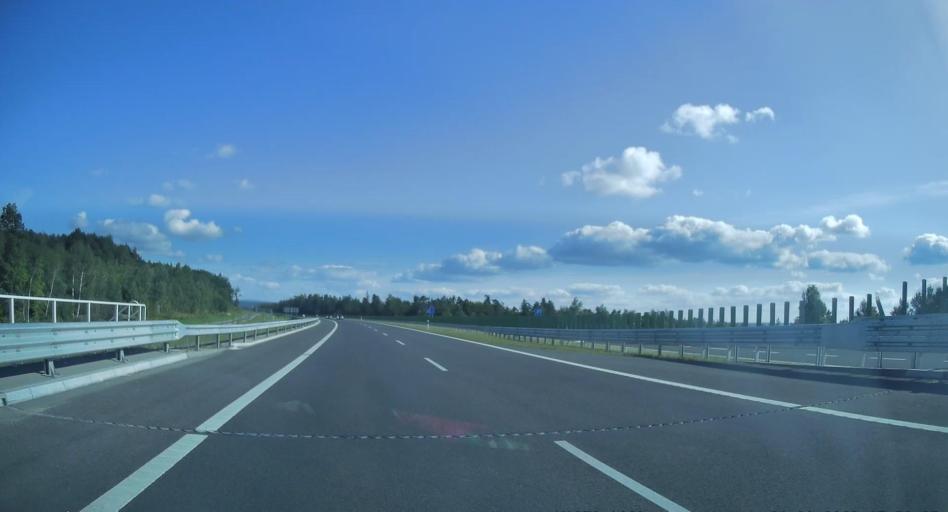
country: PL
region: Swietokrzyskie
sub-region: Powiat skarzyski
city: Skarzysko-Kamienna
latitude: 51.1353
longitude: 20.8332
